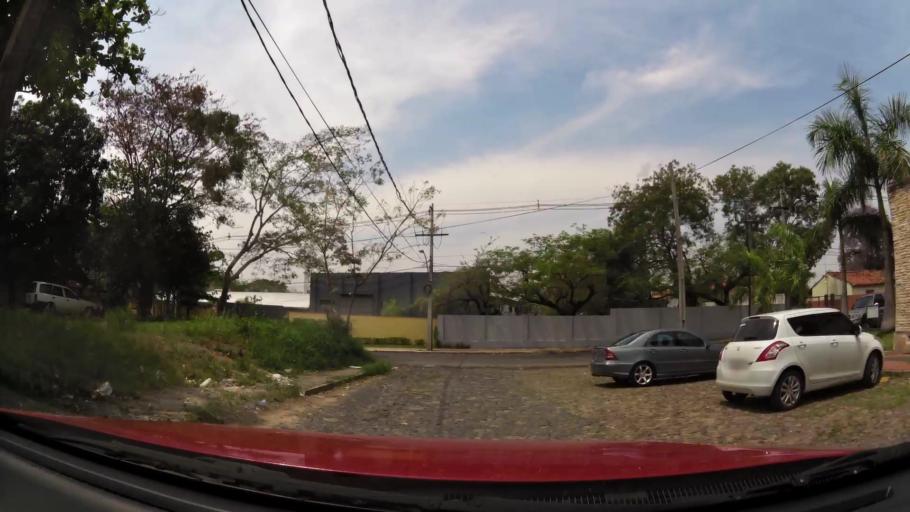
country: PY
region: Asuncion
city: Asuncion
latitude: -25.2652
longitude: -57.5936
